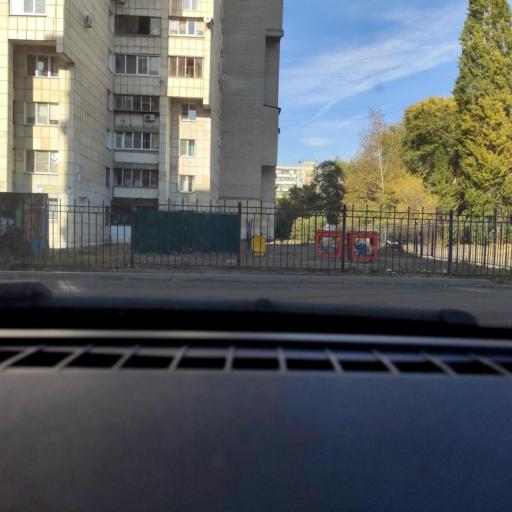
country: RU
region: Voronezj
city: Voronezh
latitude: 51.6724
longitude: 39.2456
